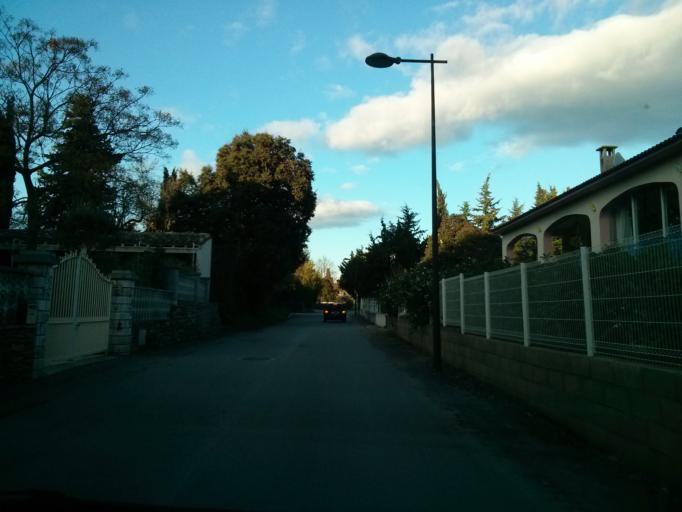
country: FR
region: Languedoc-Roussillon
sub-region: Departement du Gard
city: Aubais
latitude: 43.7547
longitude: 4.1431
